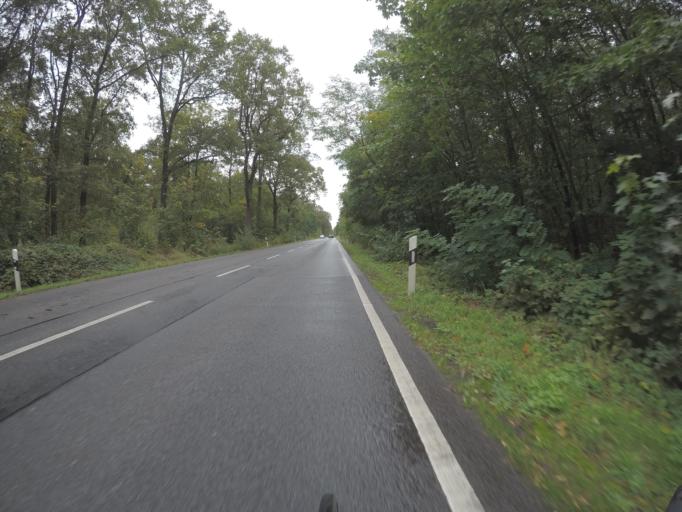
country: DE
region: Berlin
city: Buch
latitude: 52.6364
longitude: 13.4712
